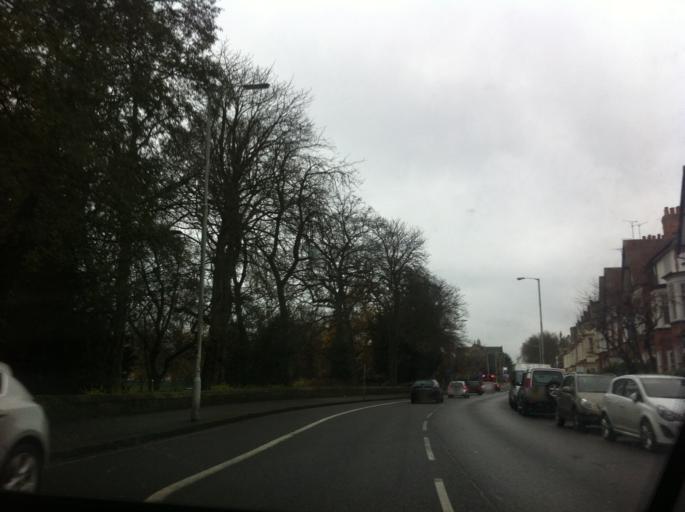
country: GB
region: England
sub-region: Northamptonshire
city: Earls Barton
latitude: 52.2647
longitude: -0.7512
